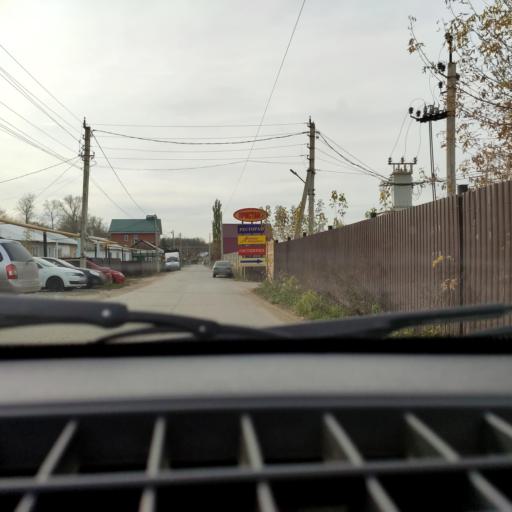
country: RU
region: Bashkortostan
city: Ufa
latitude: 54.6879
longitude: 55.9596
